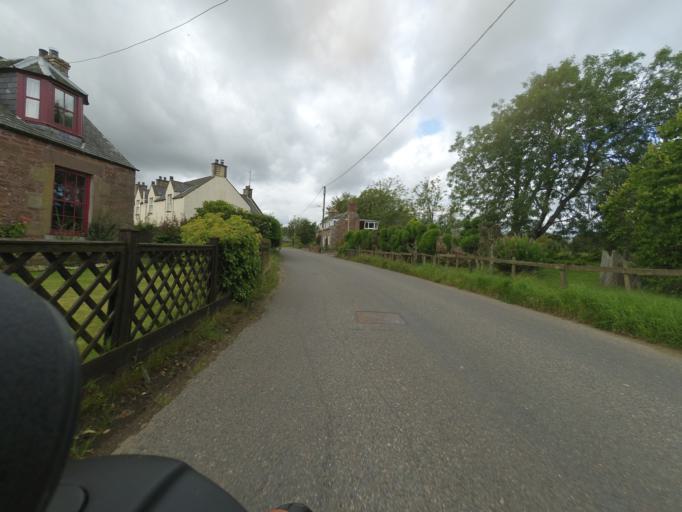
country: GB
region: Scotland
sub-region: Aberdeenshire
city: Laurencekirk
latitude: 56.8476
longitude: -2.5693
